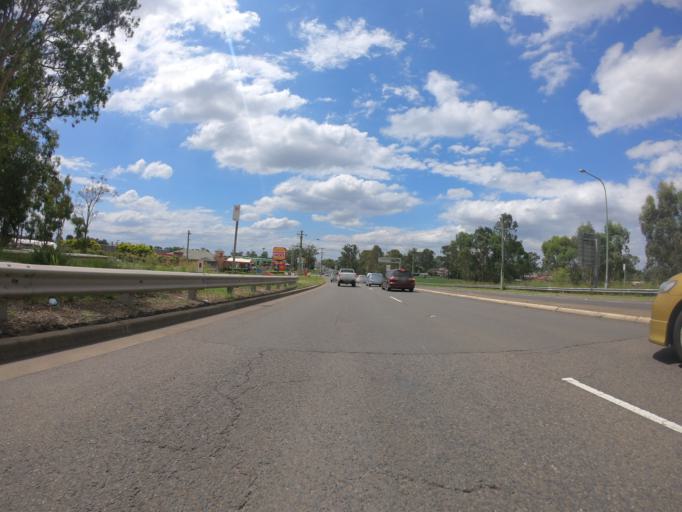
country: AU
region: New South Wales
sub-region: Blacktown
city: Mount Druitt
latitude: -33.7825
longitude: 150.7713
